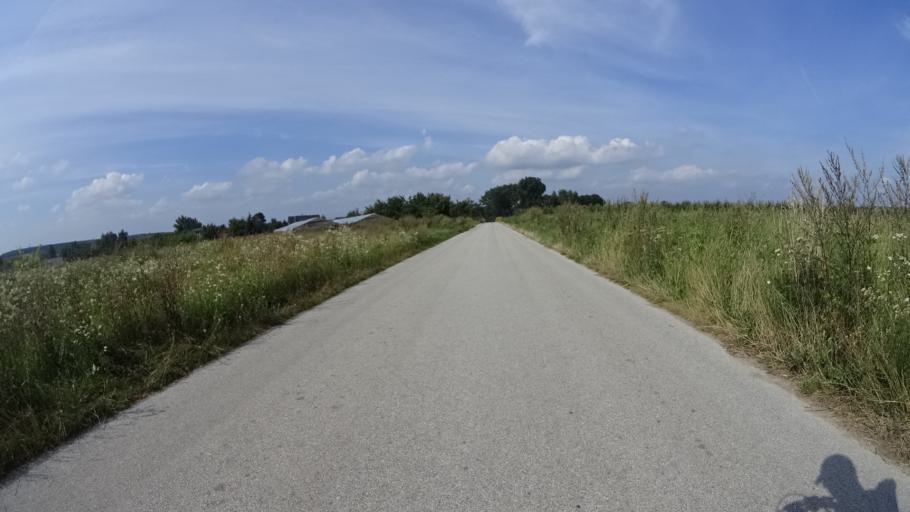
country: PL
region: Masovian Voivodeship
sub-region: Powiat grojecki
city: Goszczyn
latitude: 51.6956
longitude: 20.8475
